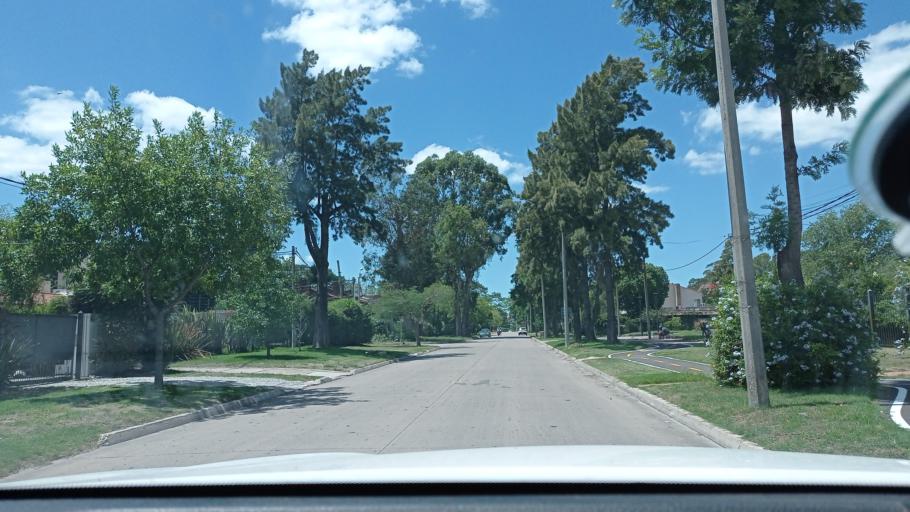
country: UY
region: Canelones
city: Paso de Carrasco
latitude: -34.8753
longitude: -56.0504
